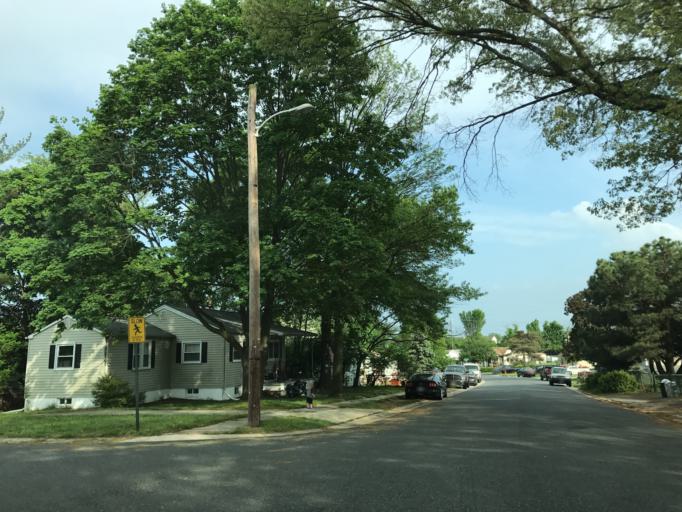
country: US
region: Maryland
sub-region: Baltimore County
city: Middle River
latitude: 39.3304
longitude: -76.4528
